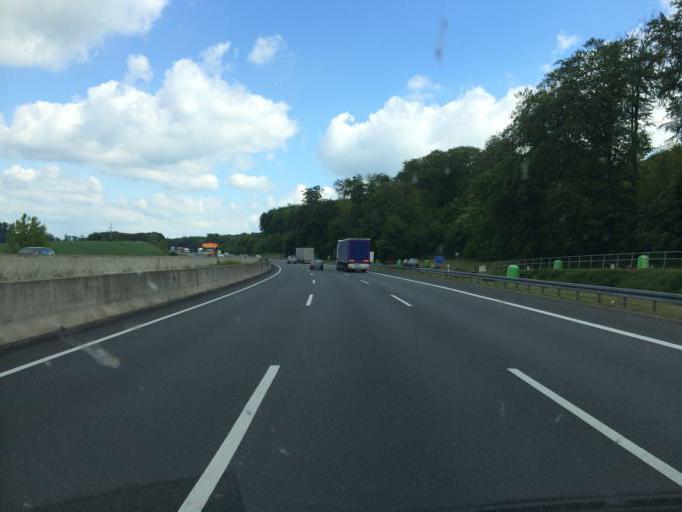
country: DE
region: Lower Saxony
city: Buchholz
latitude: 52.2163
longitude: 9.1663
